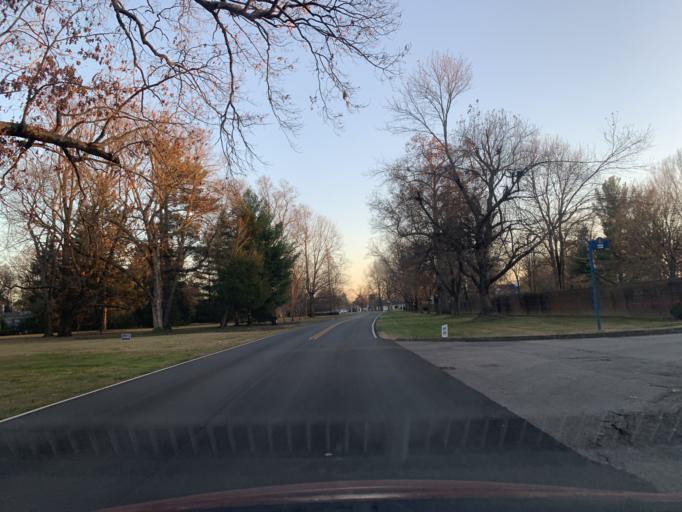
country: US
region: Kentucky
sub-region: Jefferson County
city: Saint Matthews
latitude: 38.2396
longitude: -85.6838
